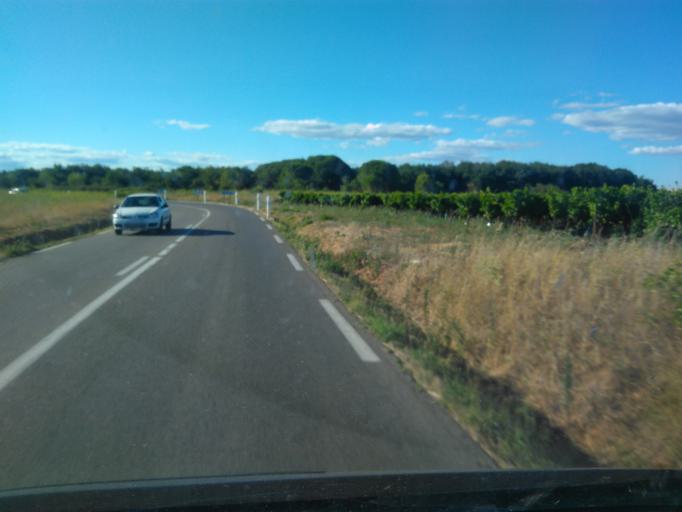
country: FR
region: Languedoc-Roussillon
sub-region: Departement du Gard
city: Vauvert
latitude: 43.6799
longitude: 4.2781
